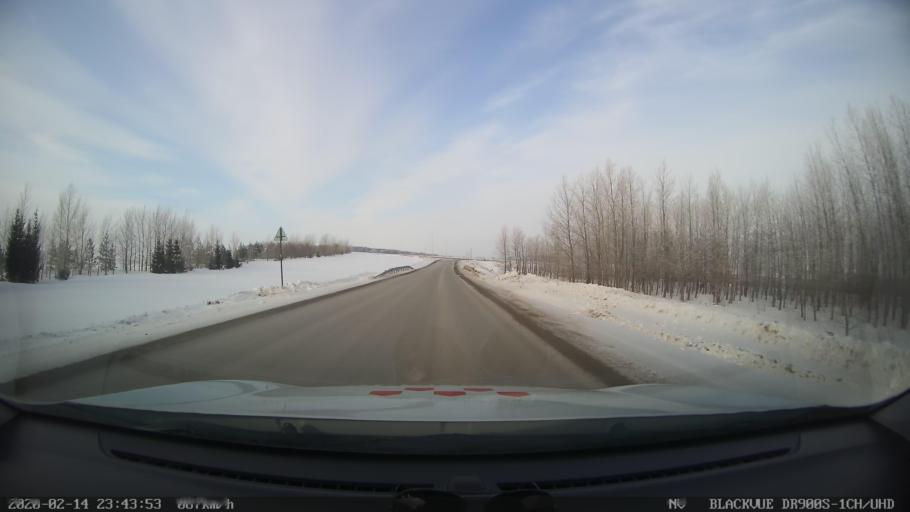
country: RU
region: Tatarstan
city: Kuybyshevskiy Zaton
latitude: 55.2074
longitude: 49.2477
